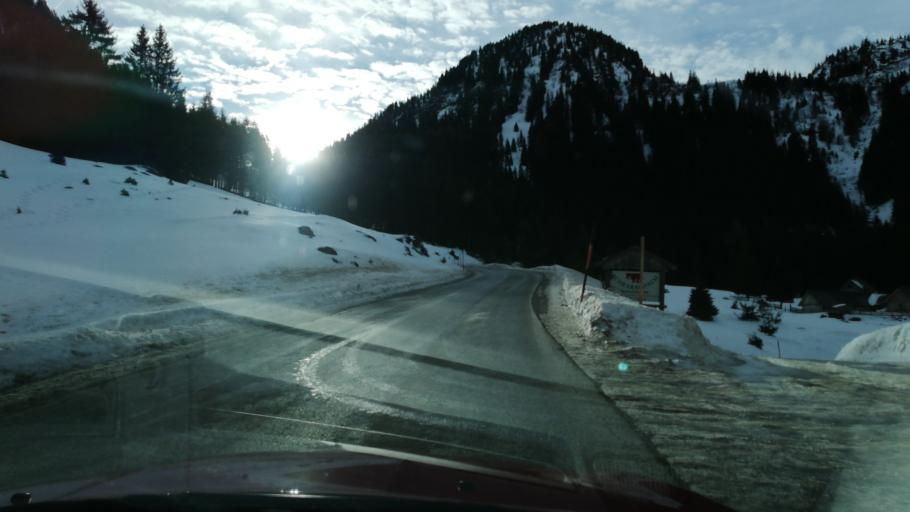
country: AT
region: Styria
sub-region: Politischer Bezirk Liezen
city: Donnersbach
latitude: 47.4134
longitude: 14.1787
